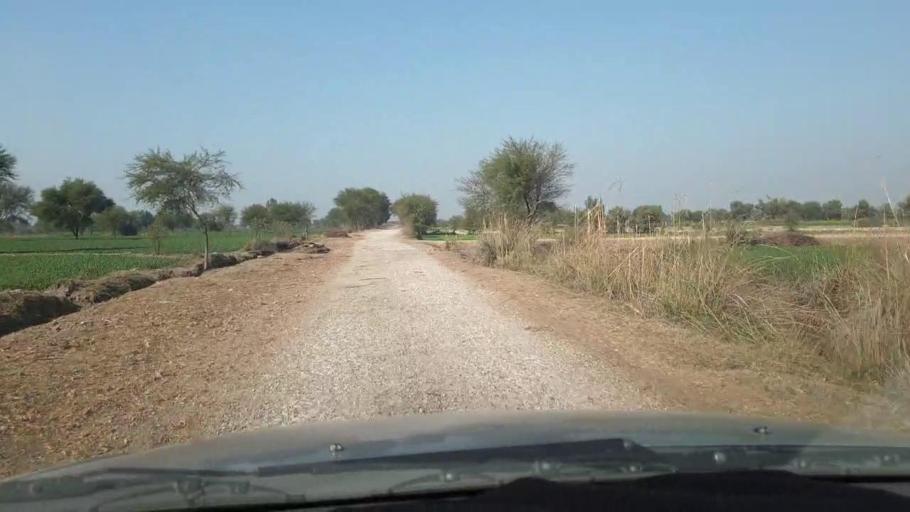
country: PK
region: Sindh
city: Mirpur Mathelo
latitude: 27.9314
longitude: 69.5631
